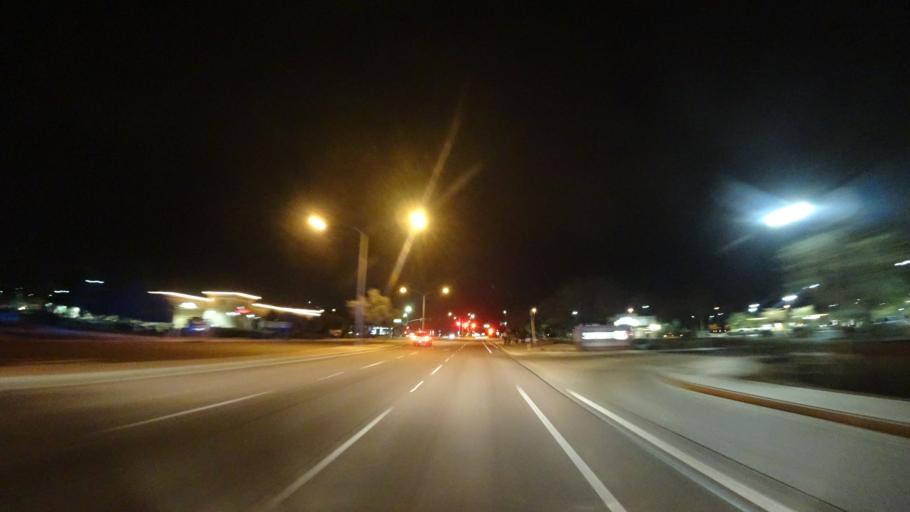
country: US
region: Arizona
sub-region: Maricopa County
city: Gilbert
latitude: 33.3792
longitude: -111.7242
